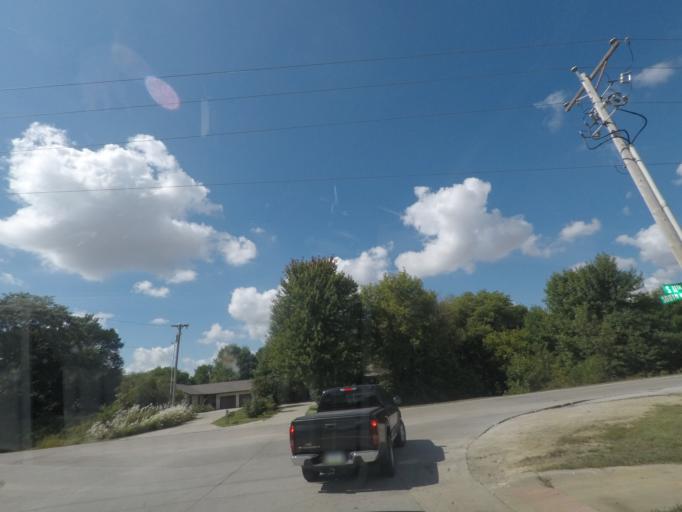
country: US
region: Iowa
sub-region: Story County
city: Nevada
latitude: 42.0098
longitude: -93.4443
